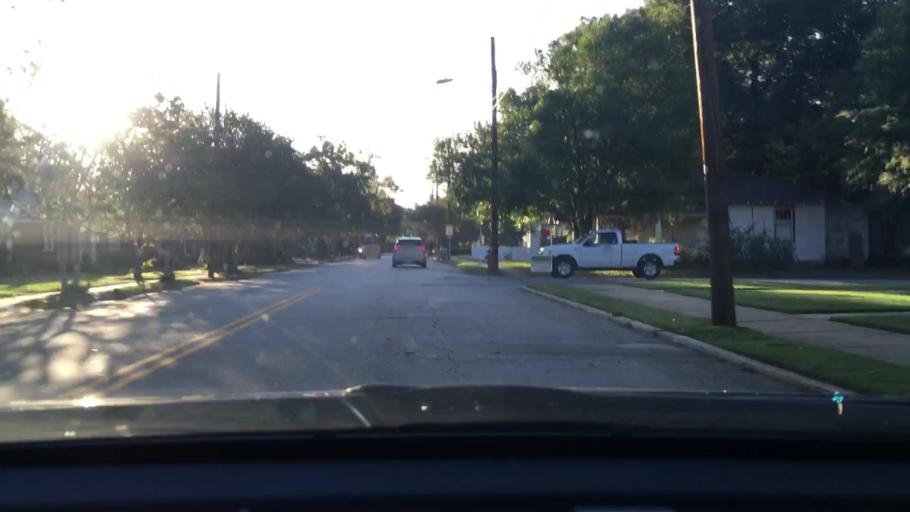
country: US
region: South Carolina
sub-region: Richland County
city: Columbia
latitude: 34.0263
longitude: -81.0521
